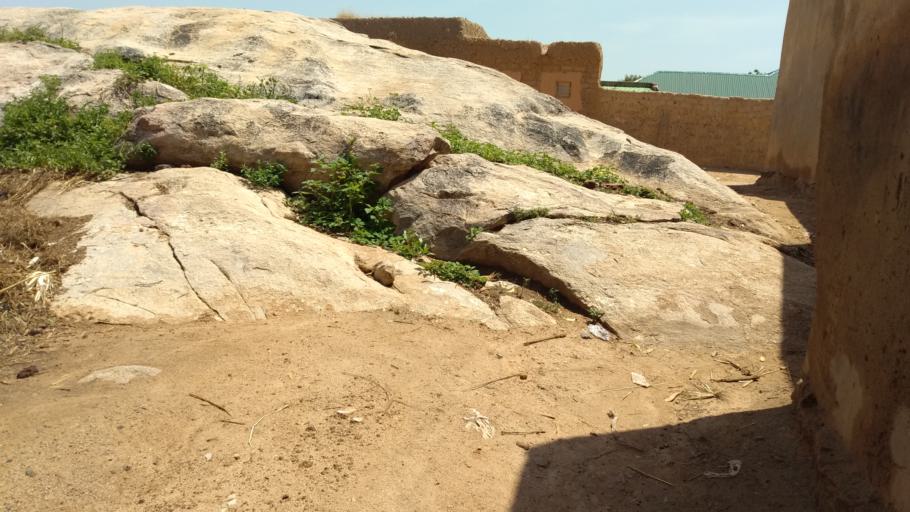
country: NG
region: Katsina
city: Kankia
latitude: 12.5067
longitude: 7.8064
